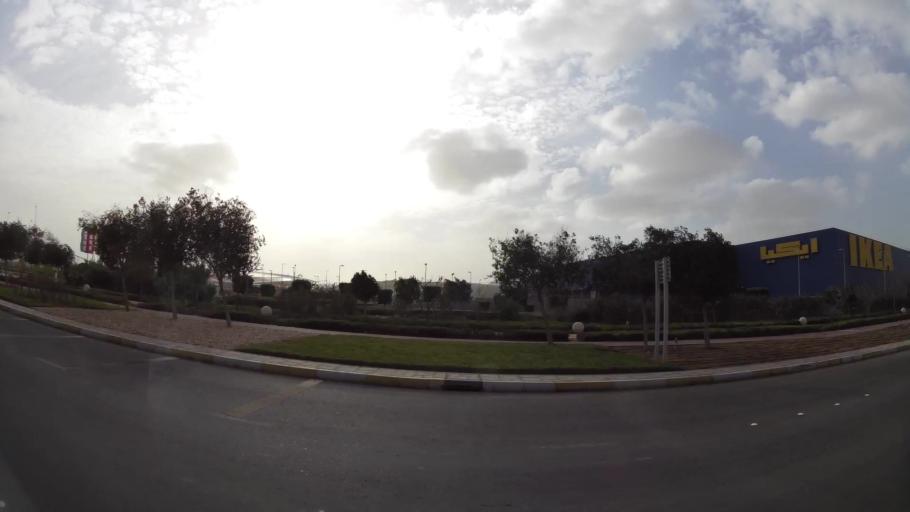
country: AE
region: Abu Dhabi
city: Abu Dhabi
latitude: 24.4888
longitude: 54.6153
